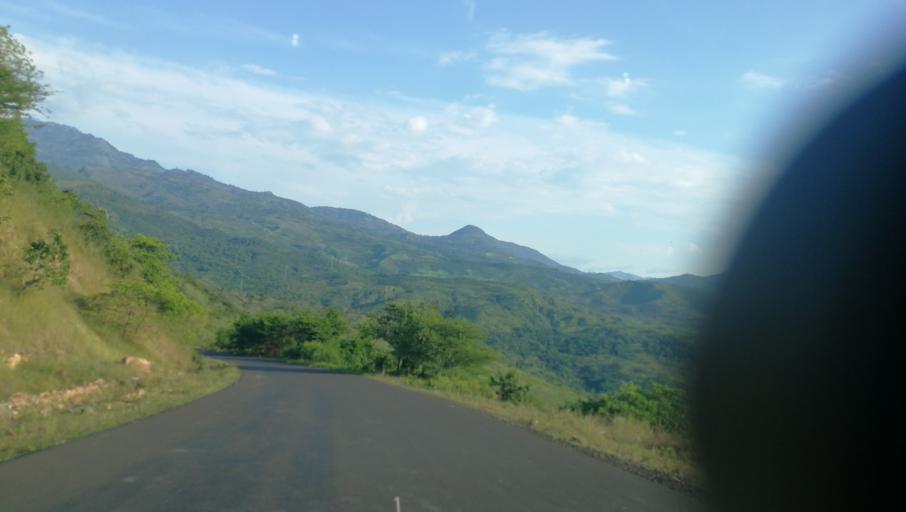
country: ET
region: Southern Nations, Nationalities, and People's Region
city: Areka
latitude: 6.8277
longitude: 37.3016
